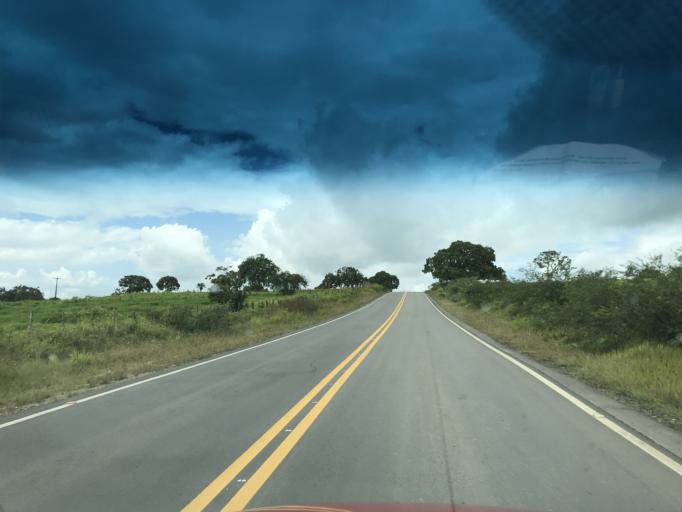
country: BR
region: Bahia
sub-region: Conceicao Do Almeida
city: Conceicao do Almeida
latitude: -12.6834
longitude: -39.2538
